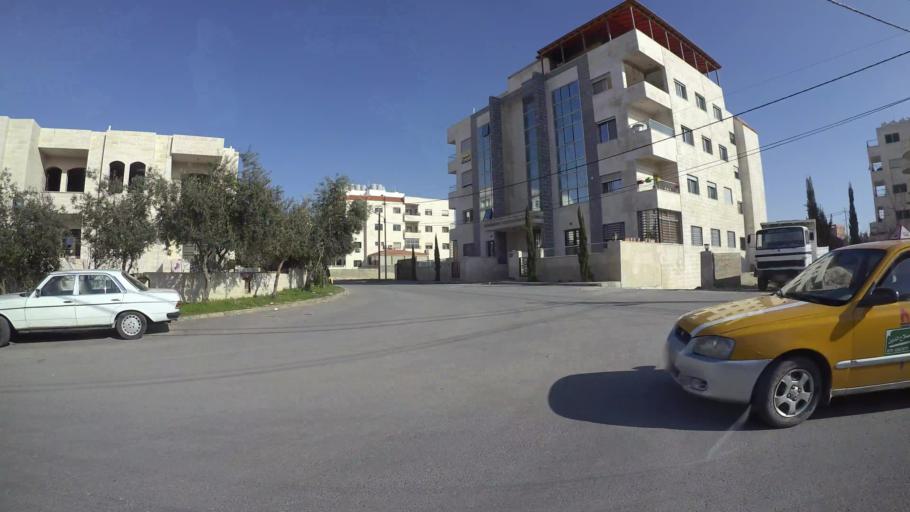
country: JO
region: Amman
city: Al Bunayyat ash Shamaliyah
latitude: 31.9016
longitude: 35.9160
